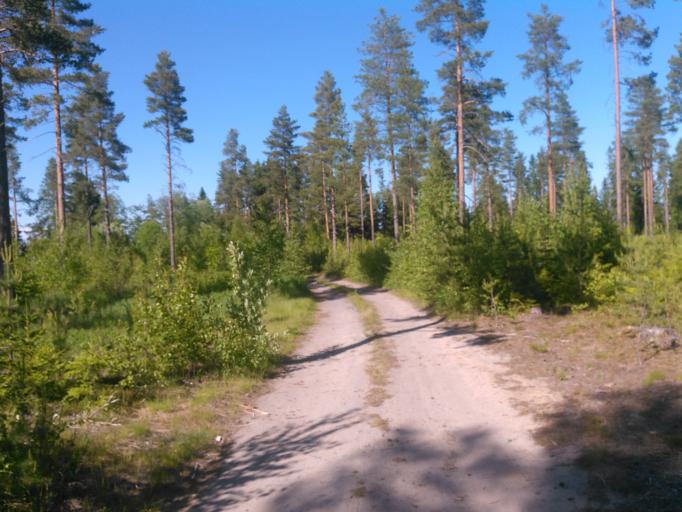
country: SE
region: Vaesterbotten
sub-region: Umea Kommun
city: Roback
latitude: 63.8254
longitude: 20.1741
